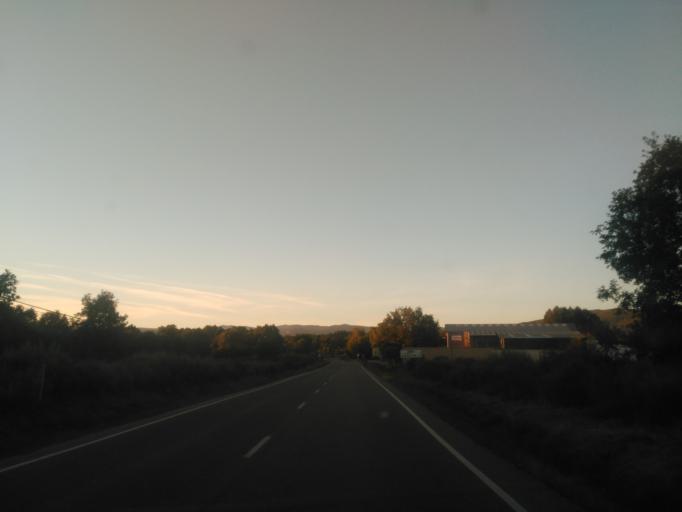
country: ES
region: Castille and Leon
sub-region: Provincia de Zamora
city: Puebla de Sanabria
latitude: 42.0679
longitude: -6.6214
